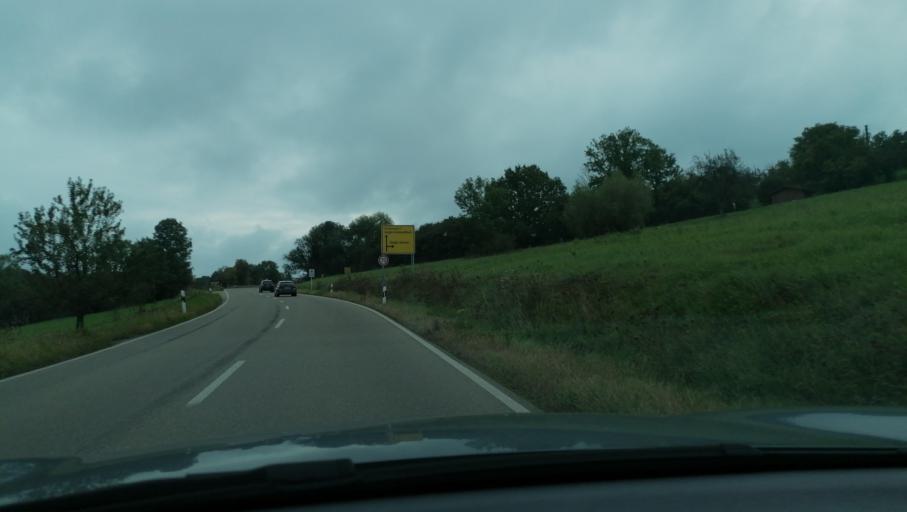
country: DE
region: Baden-Wuerttemberg
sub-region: Regierungsbezirk Stuttgart
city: Winterbach
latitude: 48.8473
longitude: 9.4673
